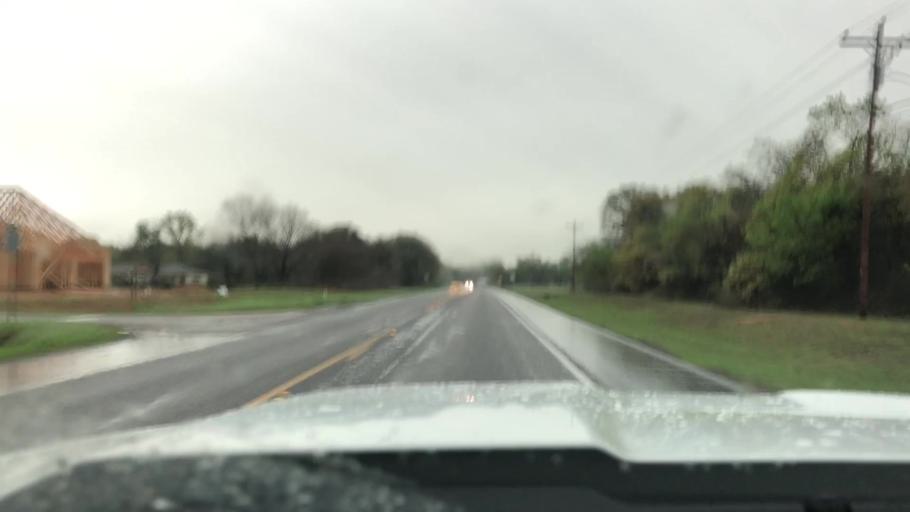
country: US
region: Texas
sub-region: Johnson County
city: Keene
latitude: 32.4312
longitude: -97.3148
